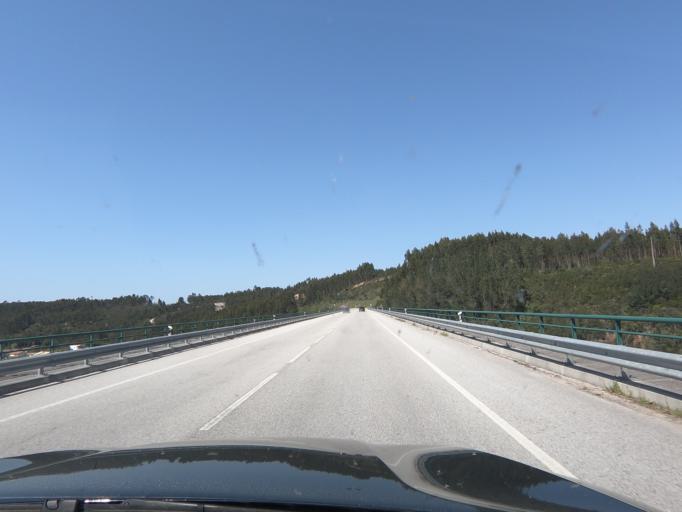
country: PT
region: Coimbra
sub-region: Lousa
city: Lousa
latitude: 40.1548
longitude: -8.2633
